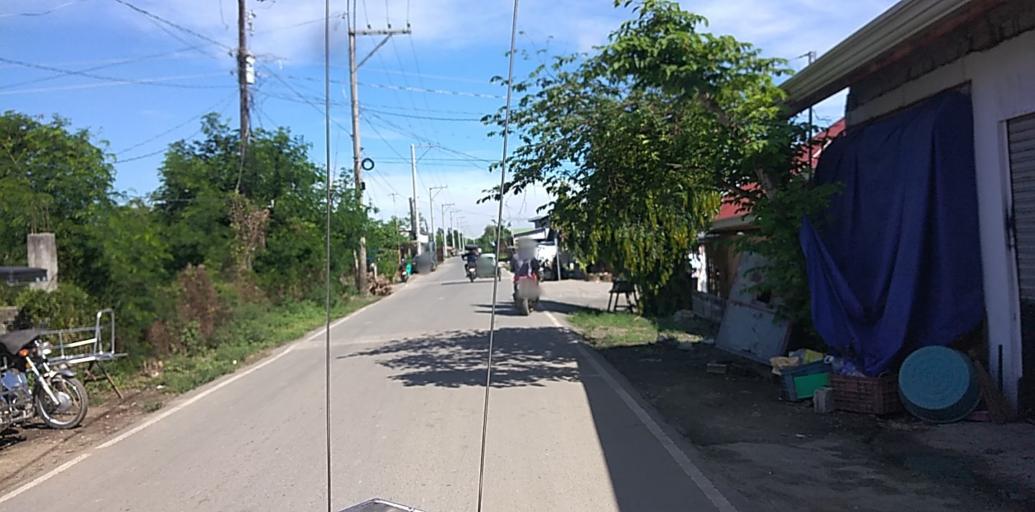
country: PH
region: Central Luzon
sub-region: Province of Pampanga
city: San Nicolas
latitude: 15.0681
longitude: 120.8054
